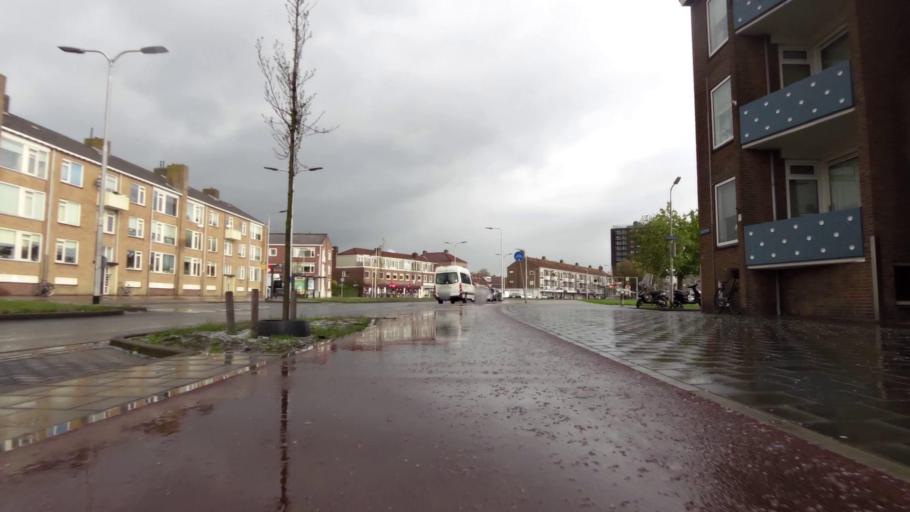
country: NL
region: North Holland
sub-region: Gemeente Velsen
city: Velsen-Zuid
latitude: 52.4549
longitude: 4.6012
